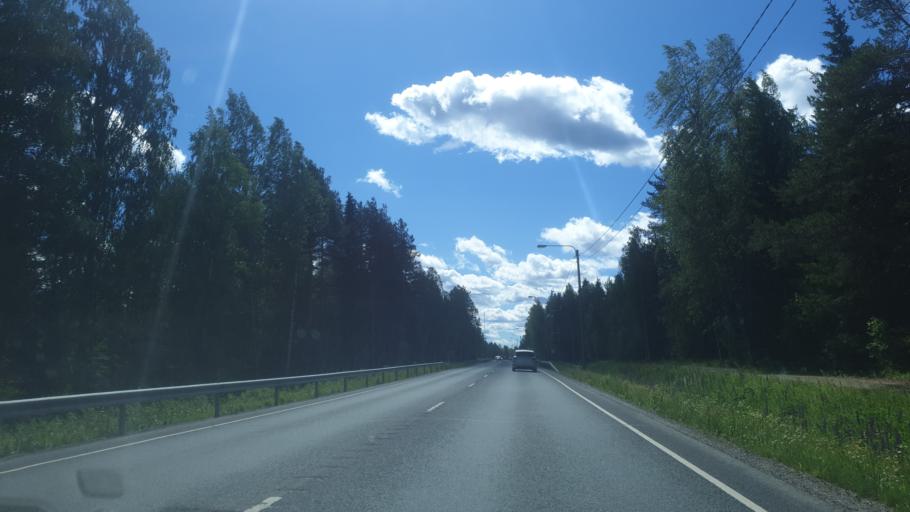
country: FI
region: Northern Savo
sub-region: Varkaus
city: Leppaevirta
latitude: 62.5904
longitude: 27.6050
